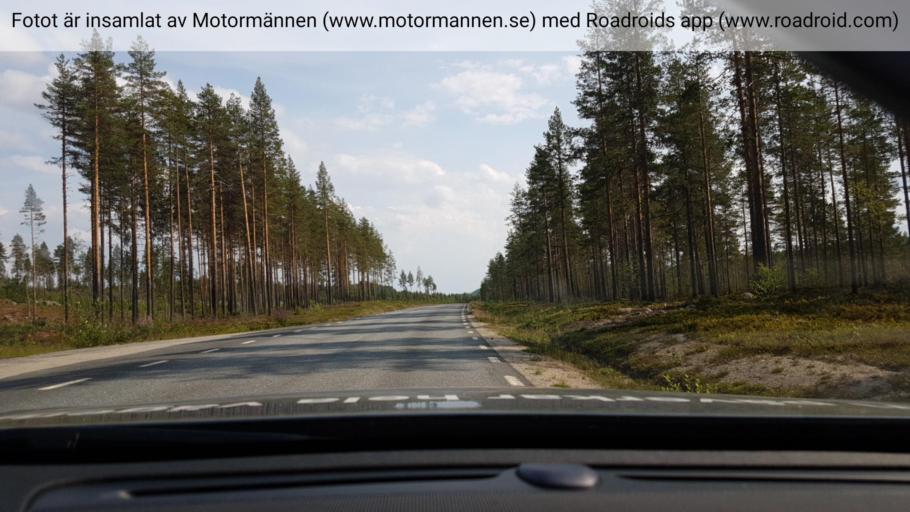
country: SE
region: Vaesterbotten
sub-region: Lycksele Kommun
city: Lycksele
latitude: 64.4156
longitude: 19.0130
